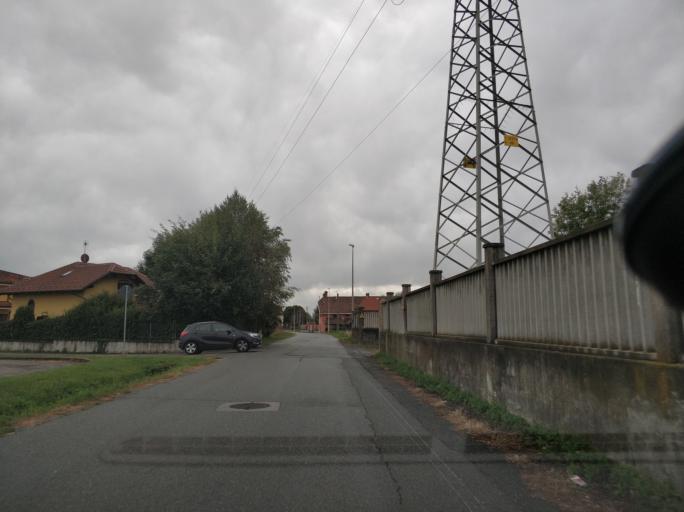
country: IT
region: Piedmont
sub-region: Provincia di Torino
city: Cirie
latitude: 45.2198
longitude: 7.5994
